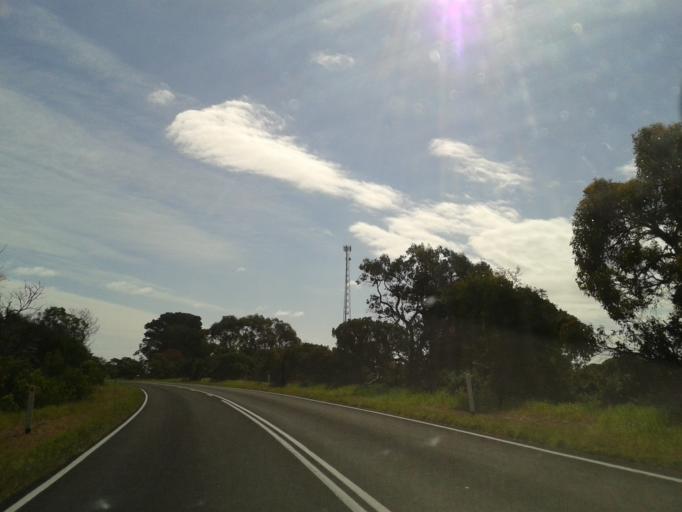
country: AU
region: Victoria
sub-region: Glenelg
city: Portland
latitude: -38.3481
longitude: 141.4999
